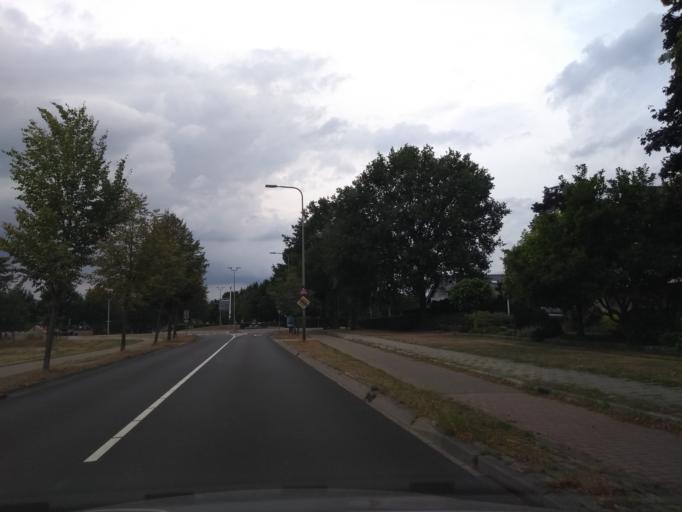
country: DE
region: Lower Saxony
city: Nordhorn
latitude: 52.3776
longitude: 6.9972
